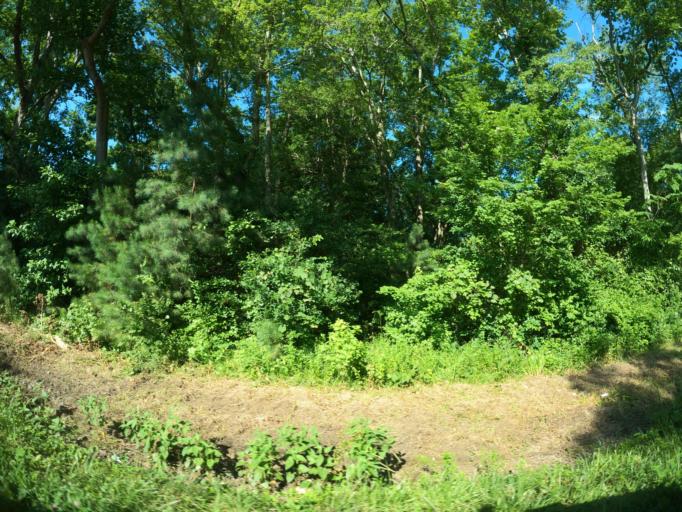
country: US
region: Delaware
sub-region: Sussex County
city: Ocean View
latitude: 38.4717
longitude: -75.1144
